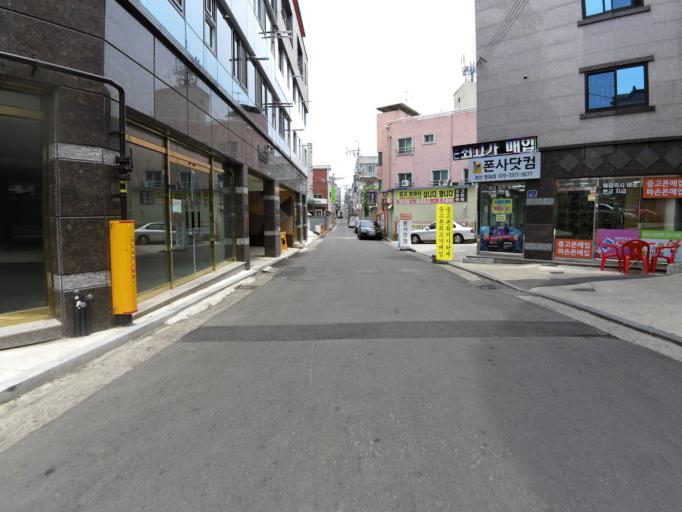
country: KR
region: Gyeongsangbuk-do
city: Gyeongsan-si
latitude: 35.8387
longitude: 128.7550
